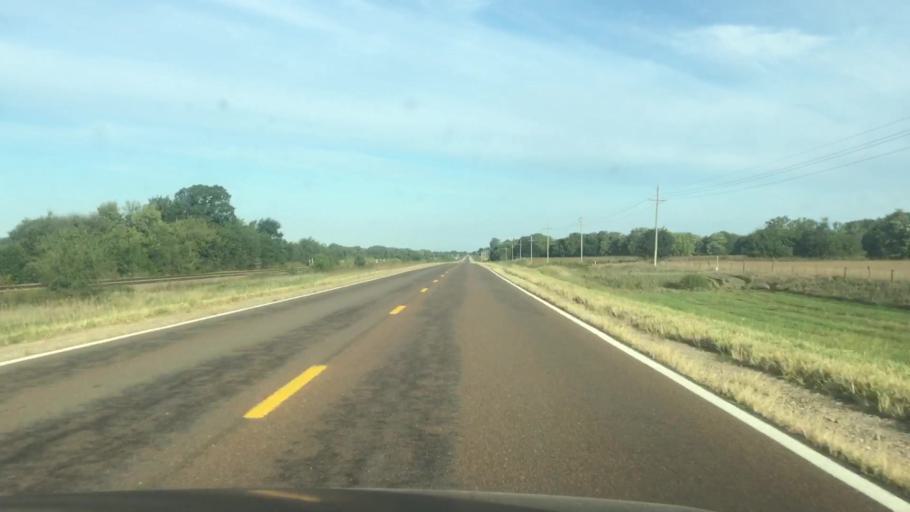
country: US
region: Nebraska
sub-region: Jefferson County
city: Fairbury
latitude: 40.0926
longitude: -97.1264
